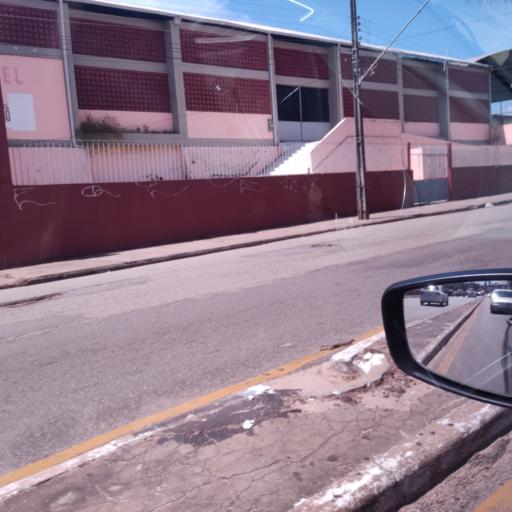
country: BR
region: Maranhao
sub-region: Sao Luis
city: Sao Luis
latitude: -2.5422
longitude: -44.2810
